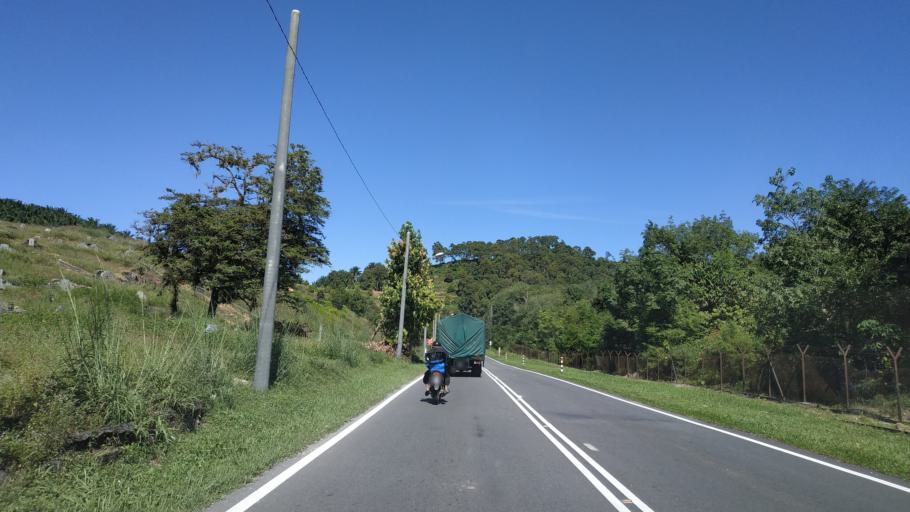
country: MY
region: Kedah
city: Kulim
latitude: 5.3249
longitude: 100.5338
